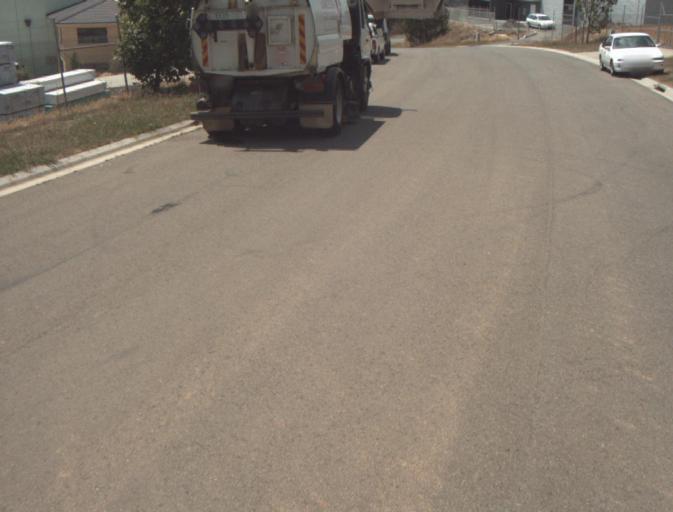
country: AU
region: Tasmania
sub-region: Launceston
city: Summerhill
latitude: -41.4929
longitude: 147.1675
